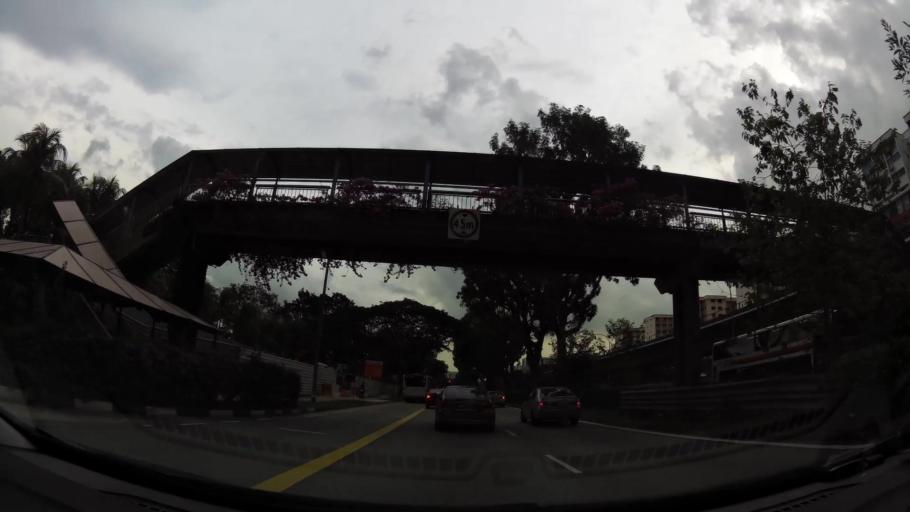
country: MY
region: Johor
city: Kampung Pasir Gudang Baru
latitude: 1.4262
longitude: 103.8352
